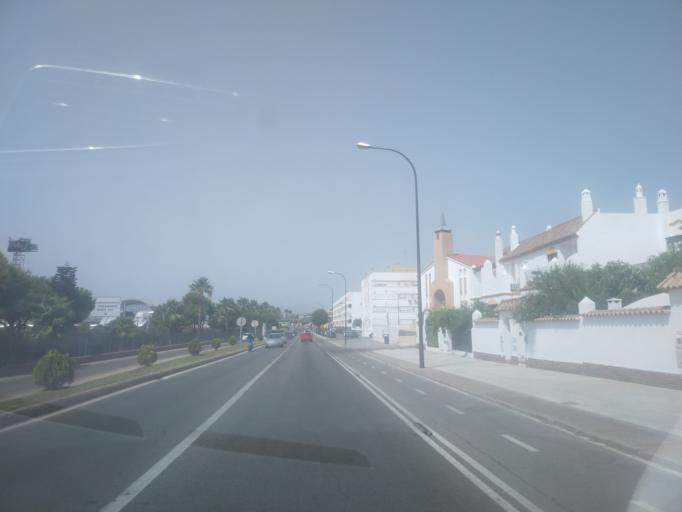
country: ES
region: Andalusia
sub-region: Provincia de Cadiz
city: San Fernando
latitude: 36.4654
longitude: -6.2075
